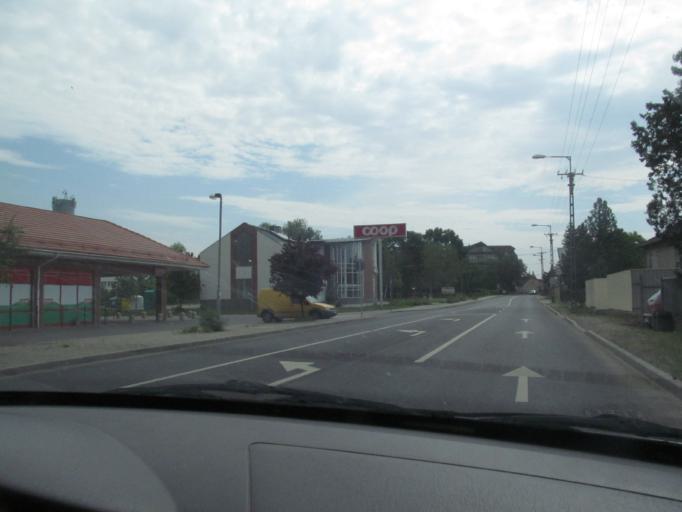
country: HU
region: Szabolcs-Szatmar-Bereg
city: Nagykallo
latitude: 47.8770
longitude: 21.8365
